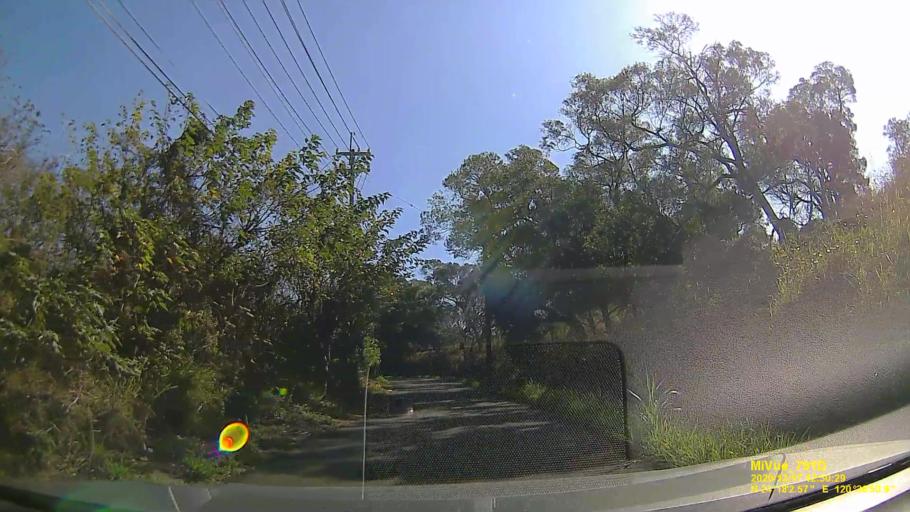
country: TW
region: Taiwan
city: Fengyuan
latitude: 24.3007
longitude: 120.6142
